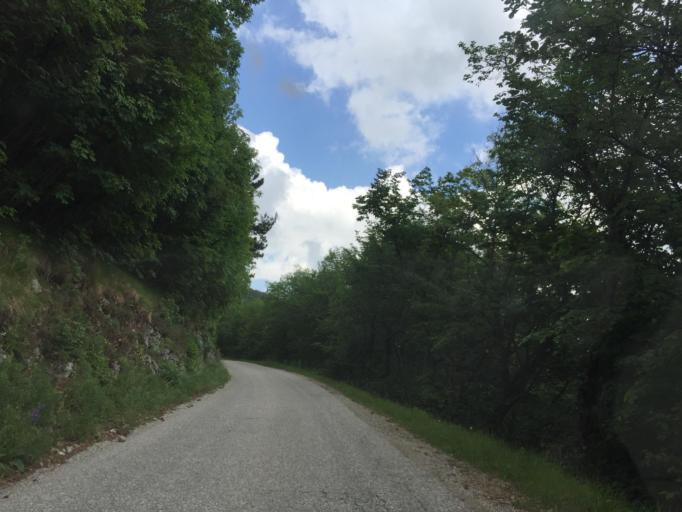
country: SI
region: Nova Gorica
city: Sempas
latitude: 46.0207
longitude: 13.7421
